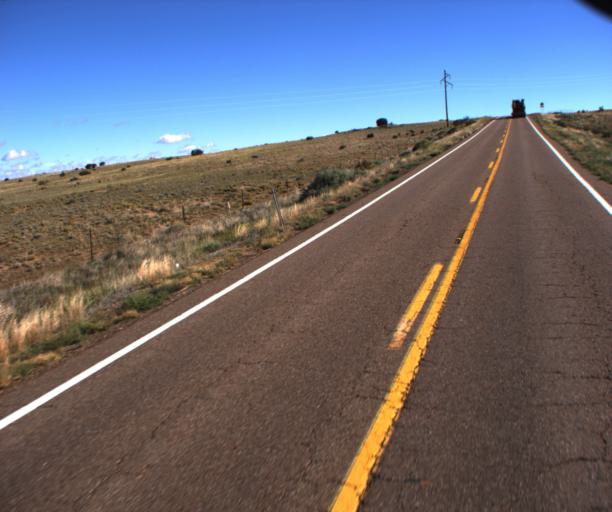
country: US
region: Arizona
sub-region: Apache County
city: Saint Johns
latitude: 34.4934
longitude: -109.5136
